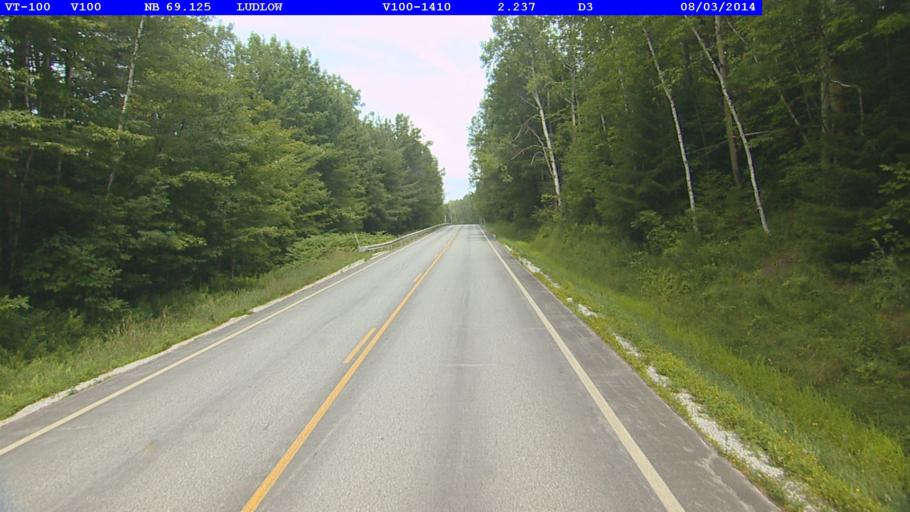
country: US
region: Vermont
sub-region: Windsor County
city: Chester
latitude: 43.3599
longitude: -72.7224
